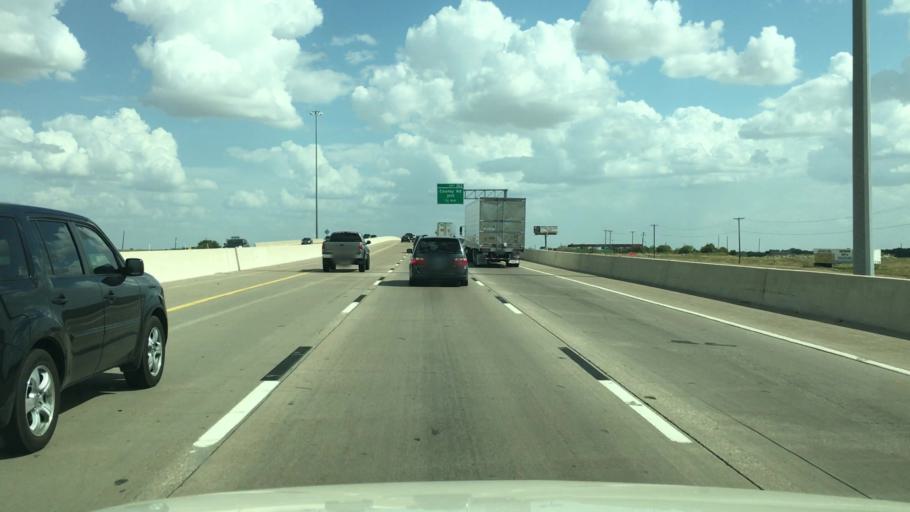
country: US
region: Texas
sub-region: Hill County
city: Hillsboro
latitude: 31.9608
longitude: -97.1171
